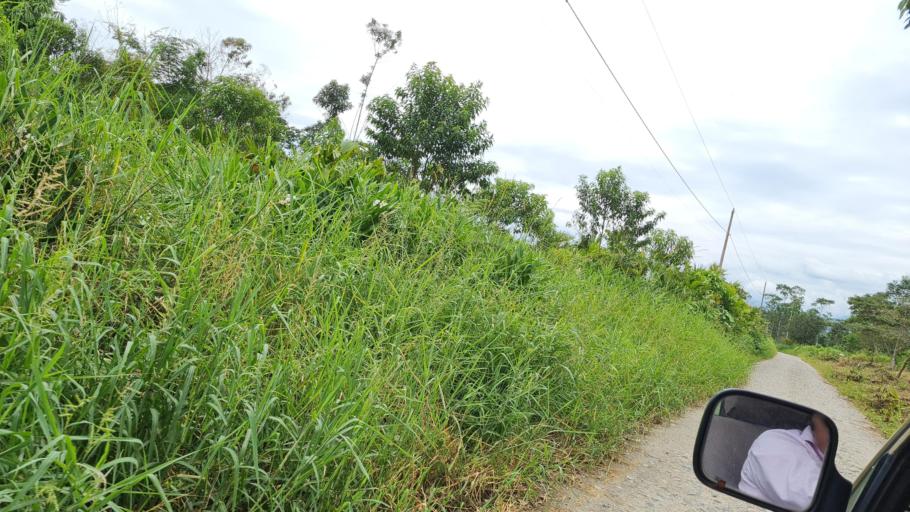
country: EC
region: Napo
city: Tena
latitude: -1.0038
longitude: -77.7721
